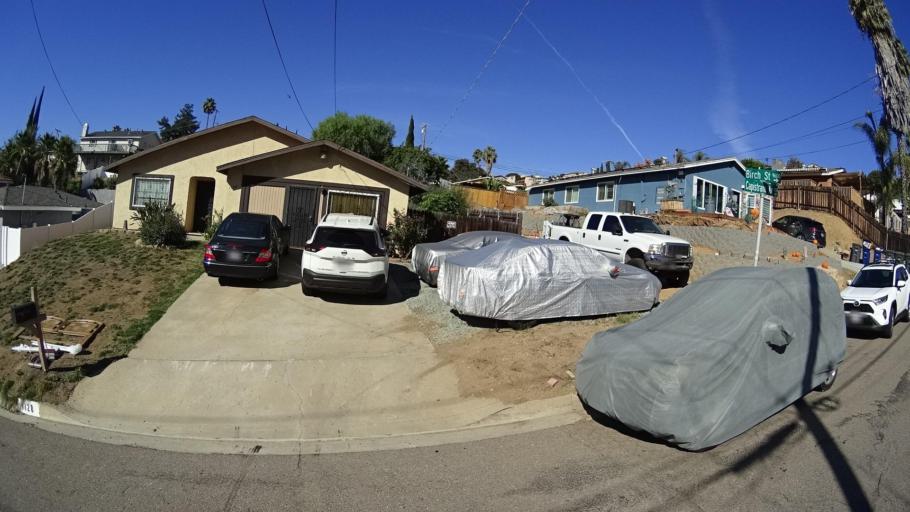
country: US
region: California
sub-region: San Diego County
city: La Presa
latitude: 32.7165
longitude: -116.9903
